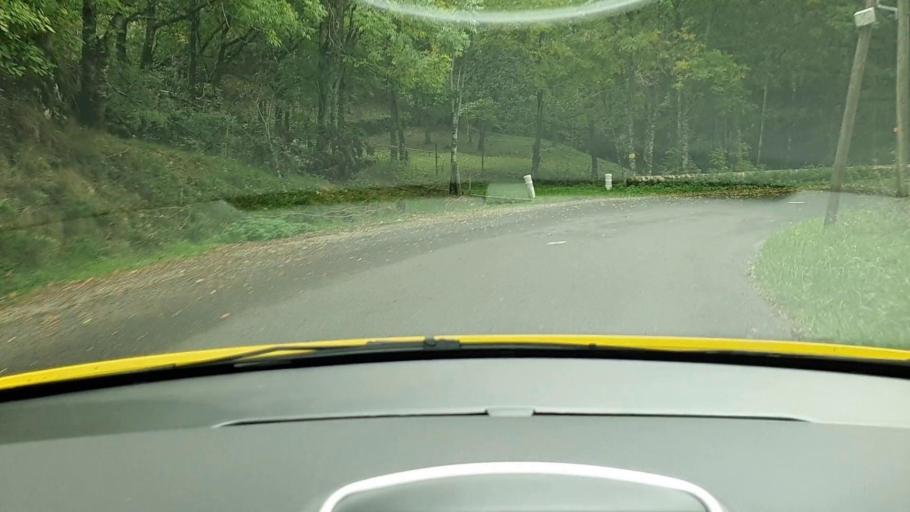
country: FR
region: Languedoc-Roussillon
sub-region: Departement de la Lozere
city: Meyrueis
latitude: 44.0604
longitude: 3.4513
